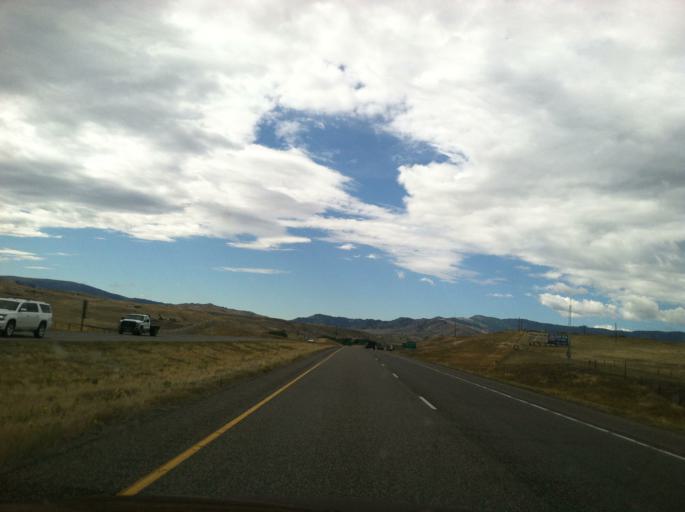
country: US
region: Montana
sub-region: Park County
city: Livingston
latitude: 45.6476
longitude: -110.5993
